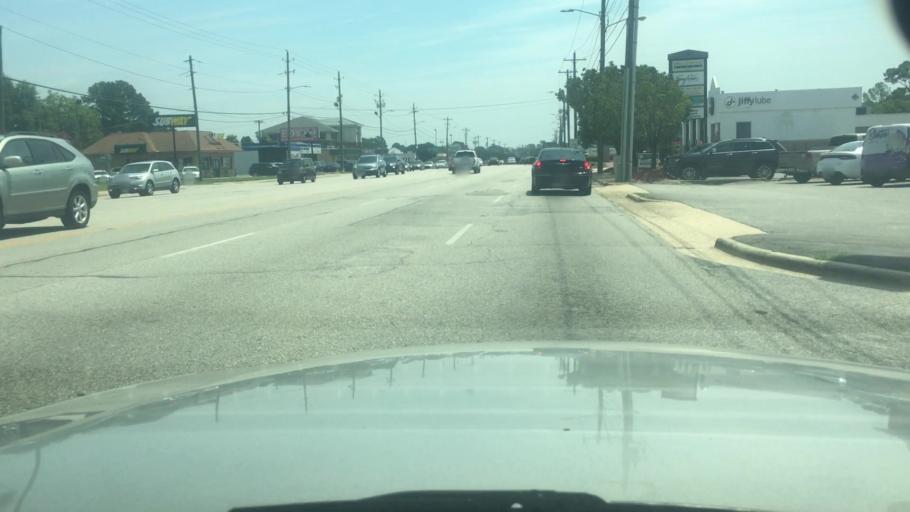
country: US
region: North Carolina
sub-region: Cumberland County
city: Fayetteville
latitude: 35.0449
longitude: -78.9290
